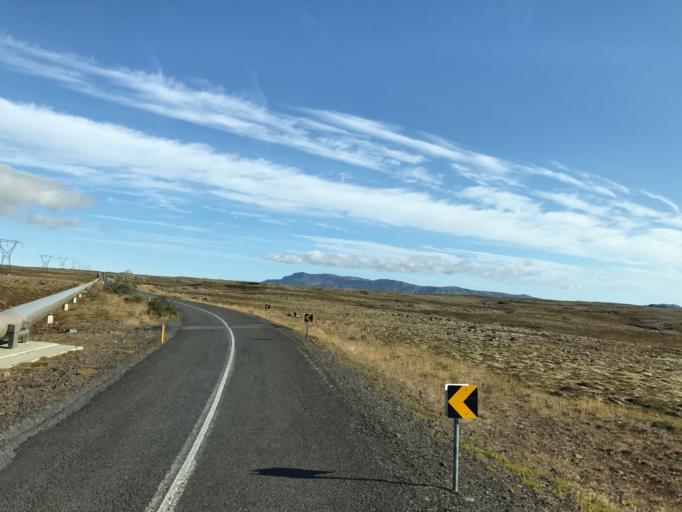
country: IS
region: Capital Region
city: Mosfellsbaer
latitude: 64.1072
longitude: -21.5953
